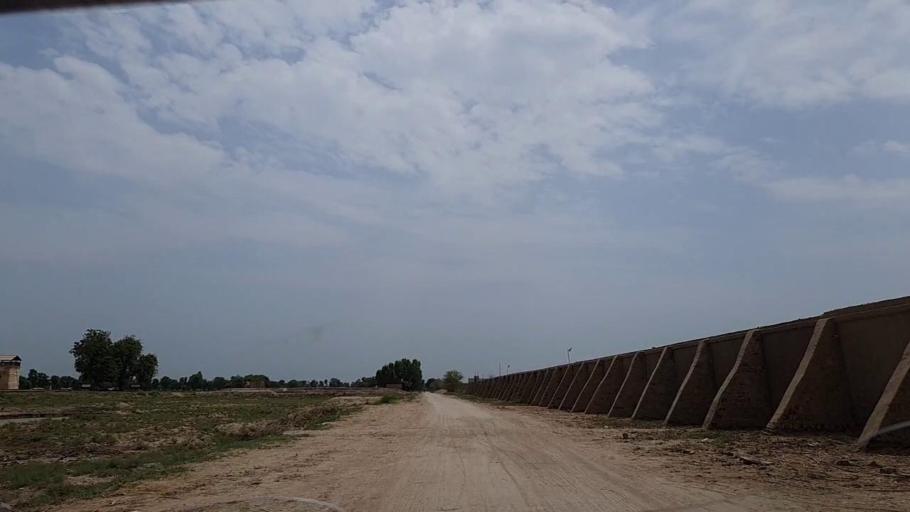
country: PK
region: Sindh
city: Tharu Shah
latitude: 26.9349
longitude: 68.1069
